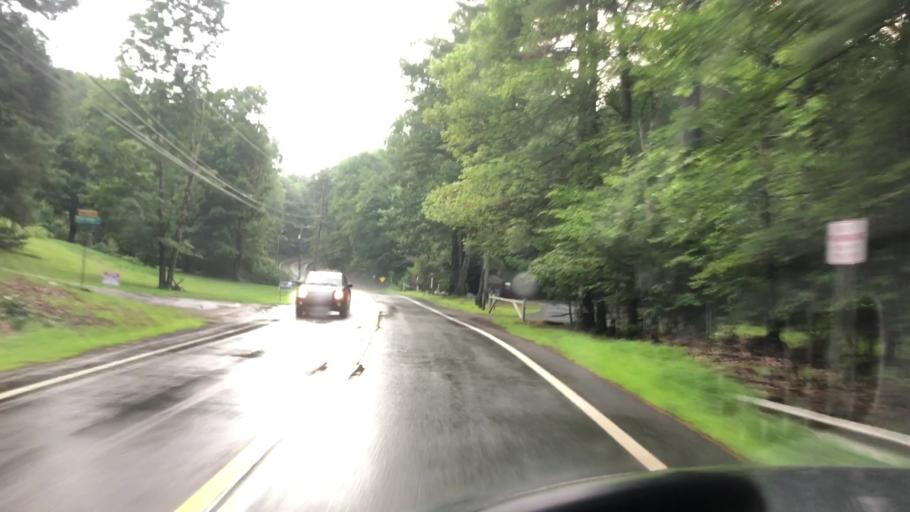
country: US
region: Massachusetts
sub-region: Hampshire County
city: Westhampton
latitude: 42.2715
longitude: -72.8645
